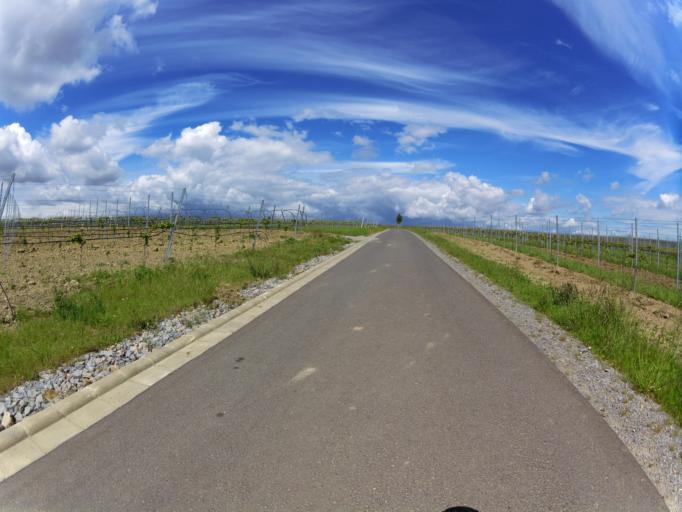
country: DE
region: Bavaria
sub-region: Regierungsbezirk Unterfranken
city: Sommerach
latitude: 49.8399
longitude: 10.1946
